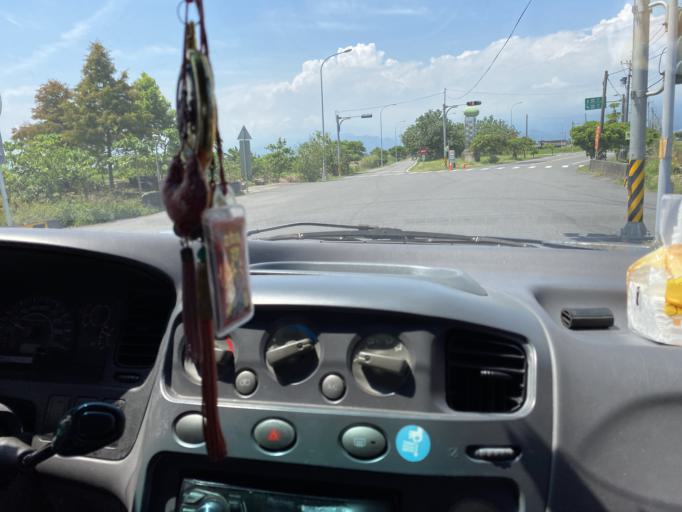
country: TW
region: Taiwan
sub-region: Yilan
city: Yilan
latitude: 24.7241
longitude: 121.8138
